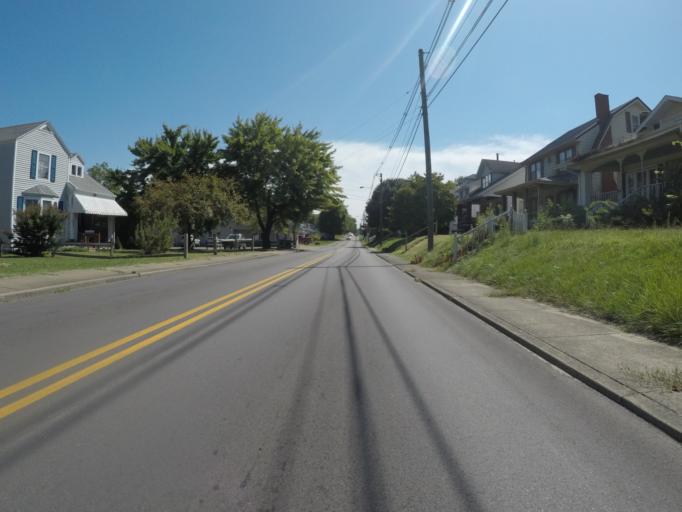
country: US
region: Kentucky
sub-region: Boyd County
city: Ashland
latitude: 38.4538
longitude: -82.6421
